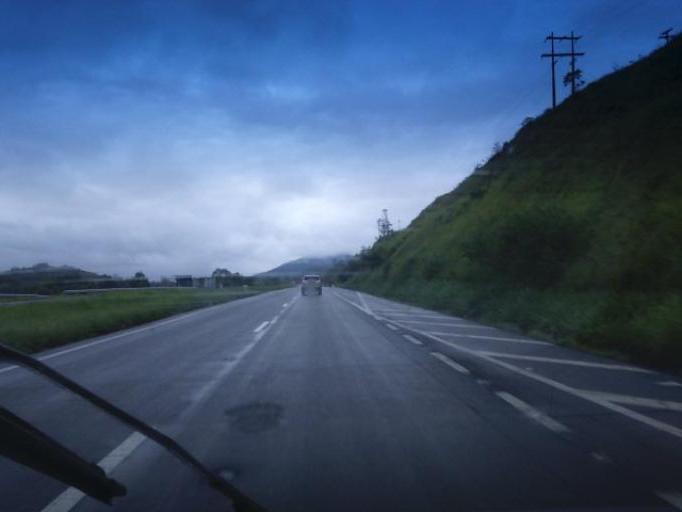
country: BR
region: Sao Paulo
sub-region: Juquia
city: Juquia
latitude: -24.3278
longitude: -47.5705
